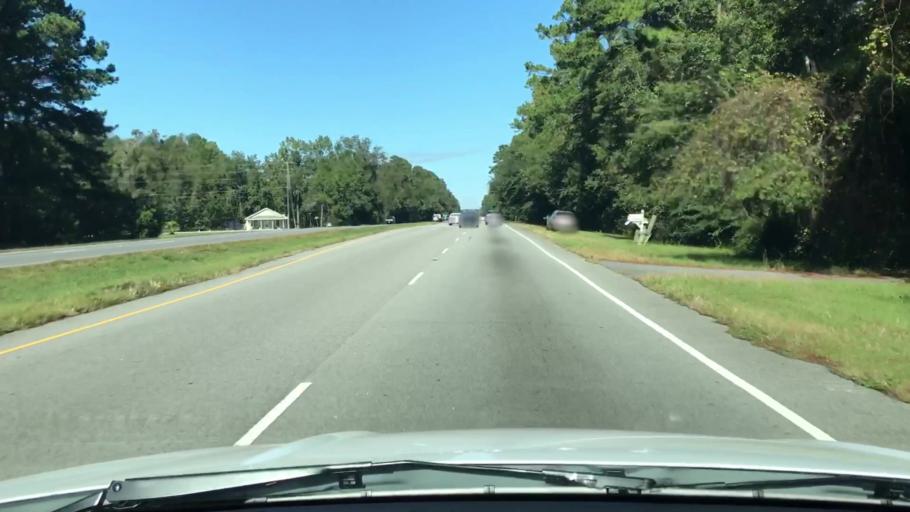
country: US
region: South Carolina
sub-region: Beaufort County
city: Laurel Bay
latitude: 32.5208
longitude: -80.7508
